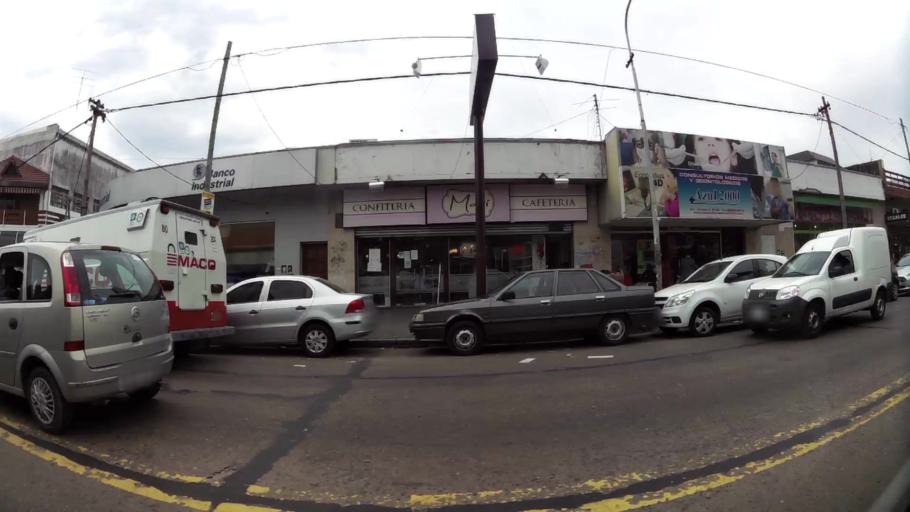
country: AR
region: Buenos Aires F.D.
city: Villa Lugano
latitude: -34.6823
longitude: -58.5145
